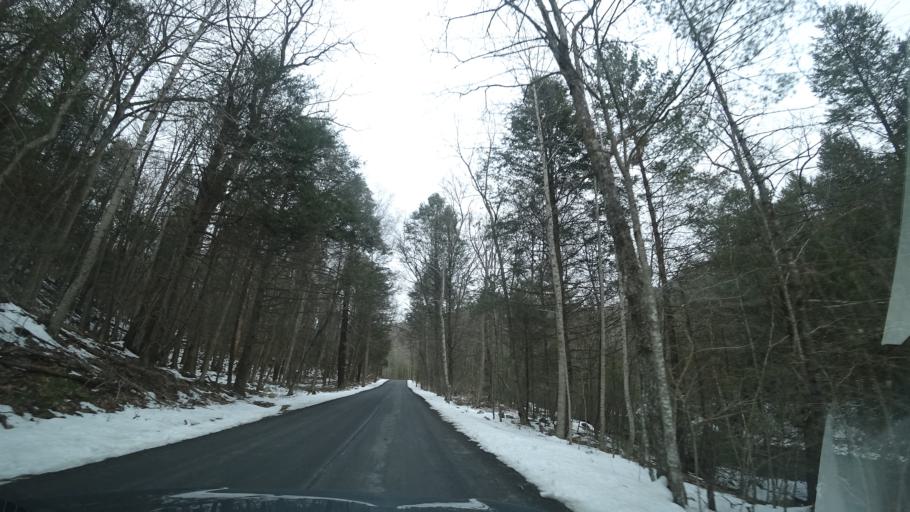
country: US
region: Virginia
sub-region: Shenandoah County
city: Woodstock
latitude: 38.9998
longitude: -78.6573
